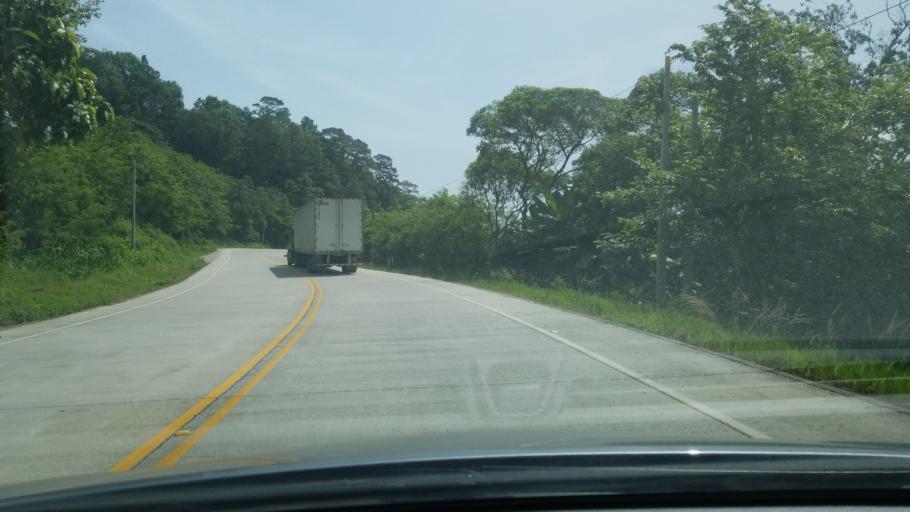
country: HN
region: Copan
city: San Jeronimo
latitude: 14.9724
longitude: -88.8897
